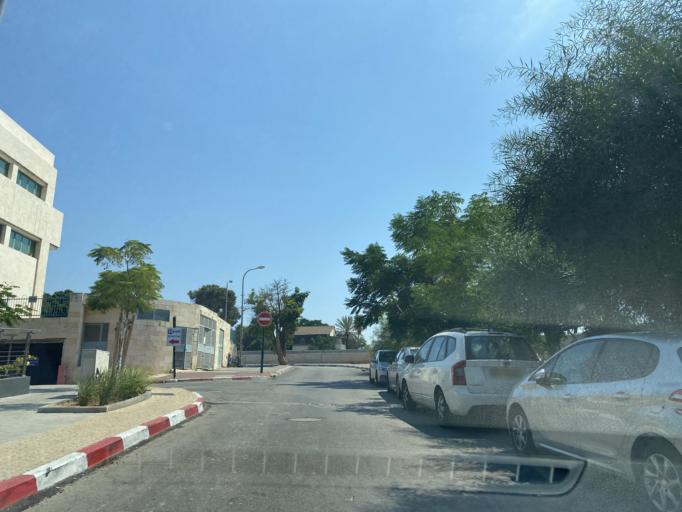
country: IL
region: Central District
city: Hod HaSharon
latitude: 32.1735
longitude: 34.8911
